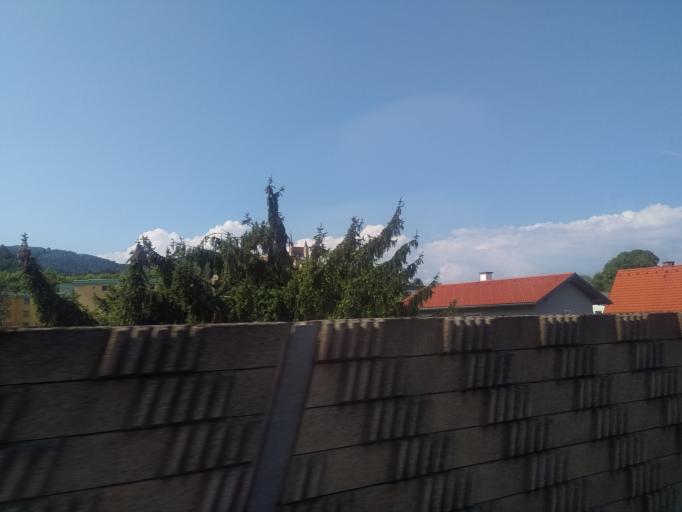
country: AT
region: Styria
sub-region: Politischer Bezirk Graz-Umgebung
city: Gratkorn
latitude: 47.1179
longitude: 15.3461
